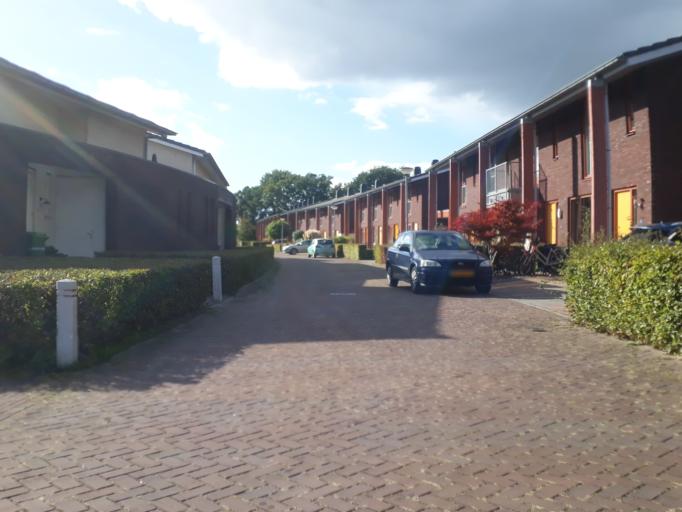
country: NL
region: Gelderland
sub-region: Gemeente Zevenaar
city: Zevenaar
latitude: 51.9241
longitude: 6.0616
